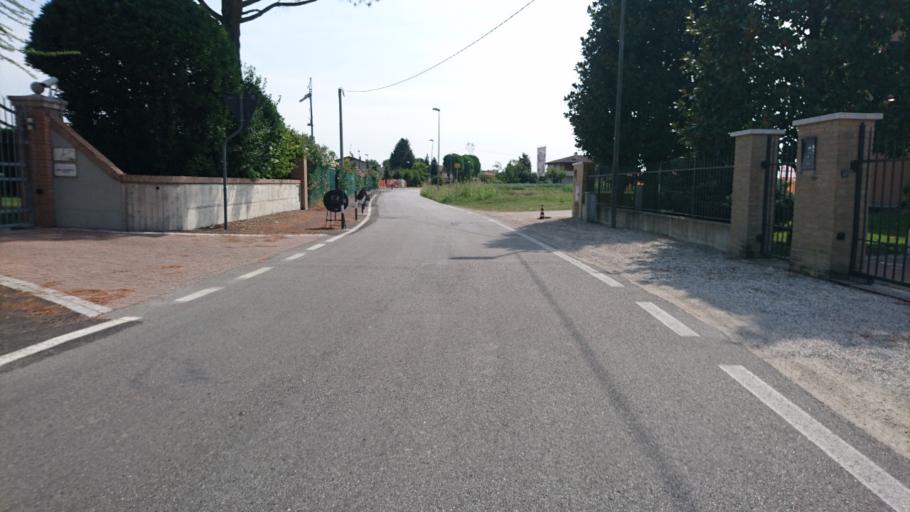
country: IT
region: Veneto
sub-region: Provincia di Padova
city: Mandriola-Sant'Agostino
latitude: 45.3636
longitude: 11.8500
